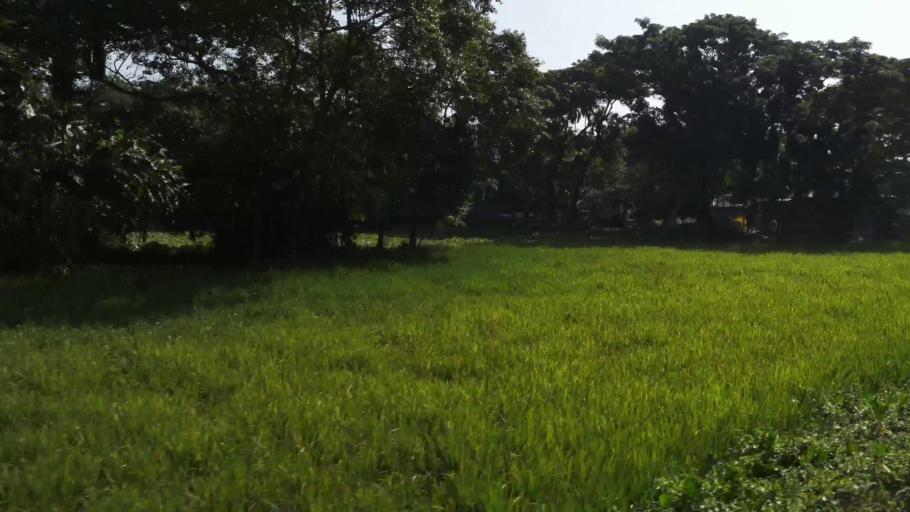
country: BD
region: Dhaka
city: Gafargaon
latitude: 24.5917
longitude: 90.5032
